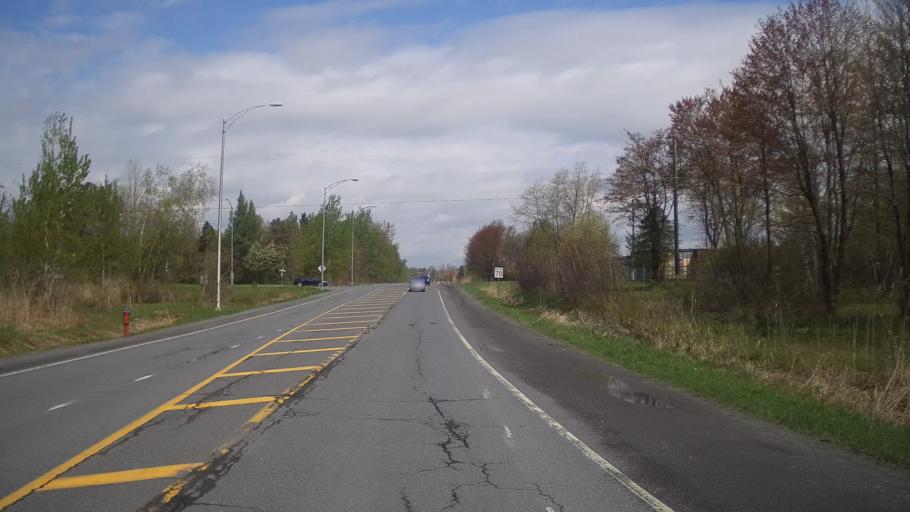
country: CA
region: Quebec
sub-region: Monteregie
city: Cowansville
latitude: 45.1987
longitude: -72.7635
